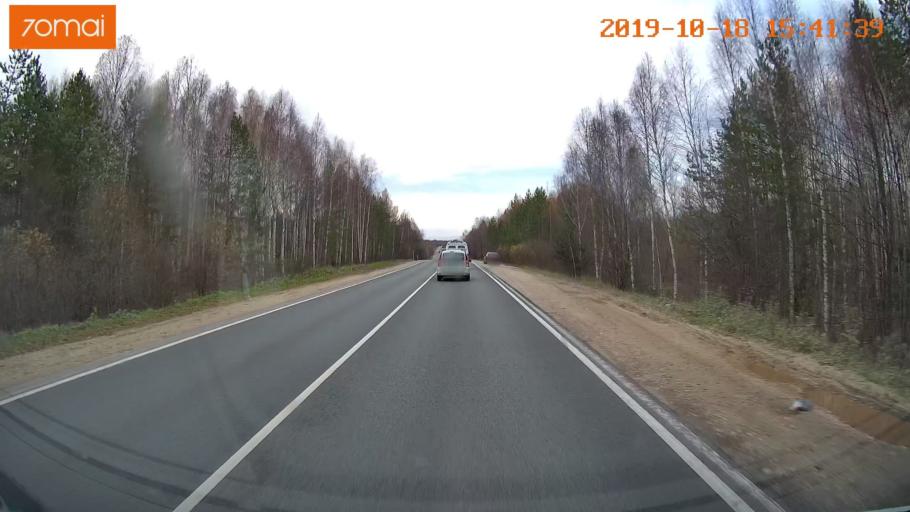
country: RU
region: Vladimir
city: Golovino
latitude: 55.9479
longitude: 40.5798
